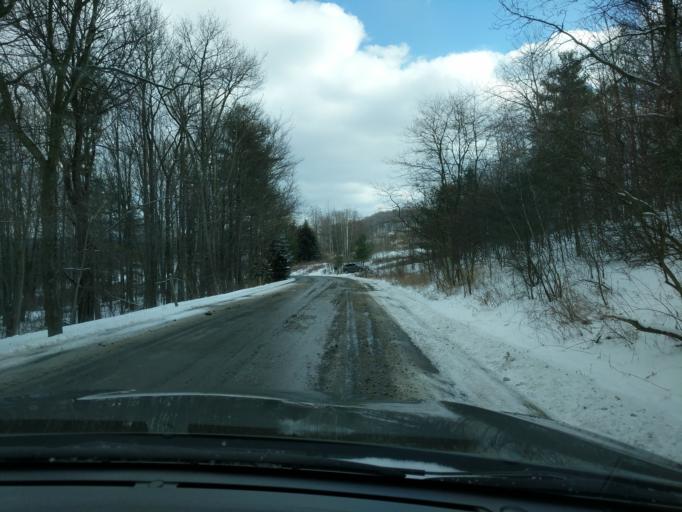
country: US
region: New York
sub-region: Tompkins County
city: East Ithaca
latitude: 42.4287
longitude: -76.4343
